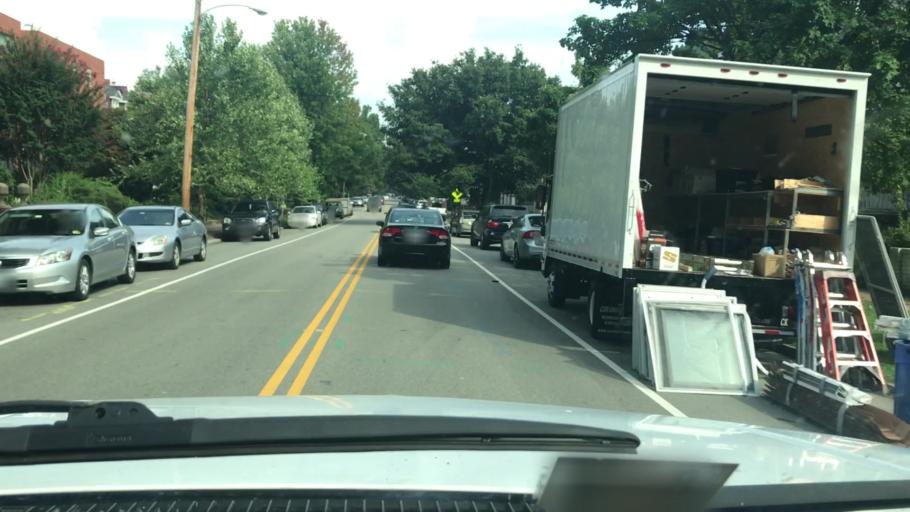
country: US
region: Virginia
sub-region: City of Richmond
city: Richmond
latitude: 37.5583
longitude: -77.4839
